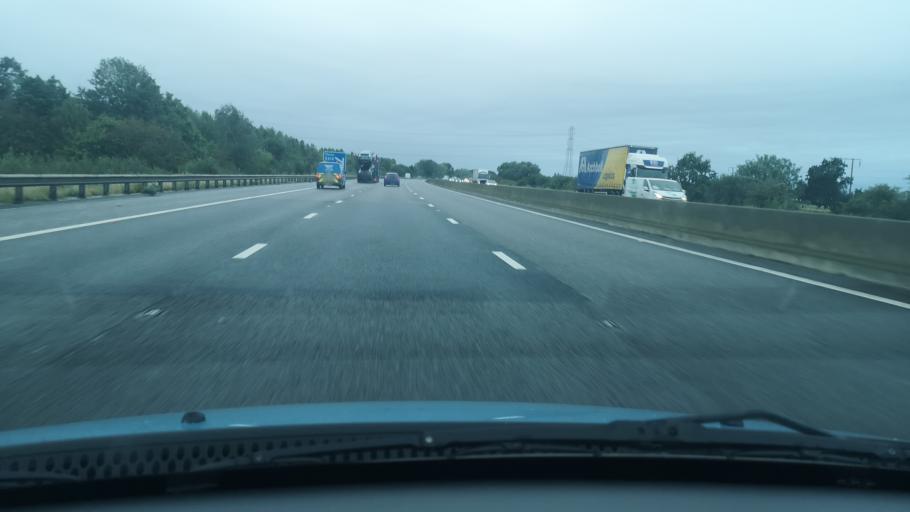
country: GB
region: England
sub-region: East Riding of Yorkshire
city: Rawcliffe
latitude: 53.6300
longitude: -0.9677
